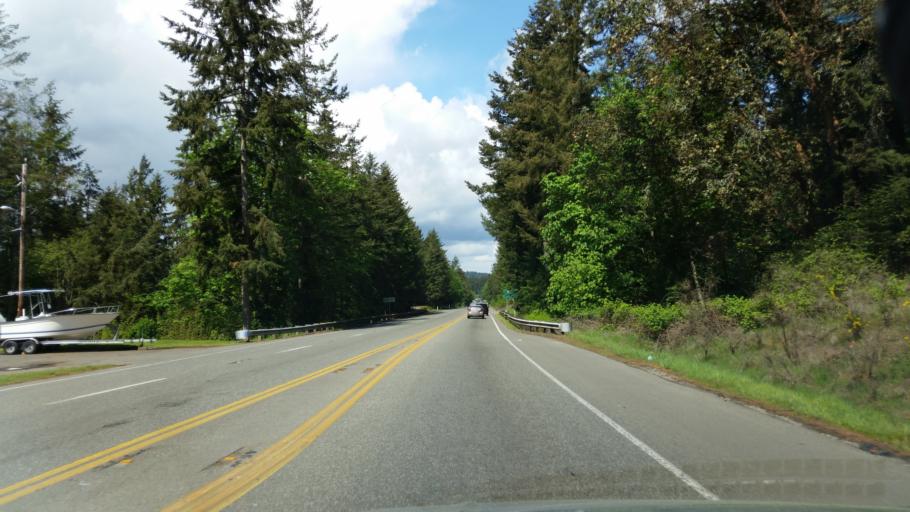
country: US
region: Washington
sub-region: Pierce County
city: Purdy
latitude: 47.3756
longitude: -122.6223
